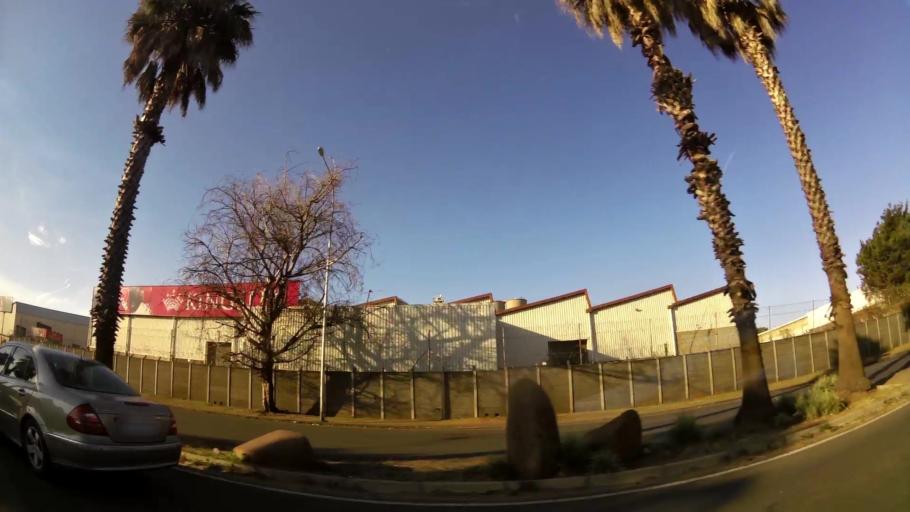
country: ZA
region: Gauteng
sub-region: City of Johannesburg Metropolitan Municipality
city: Roodepoort
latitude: -26.1553
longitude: 27.8668
